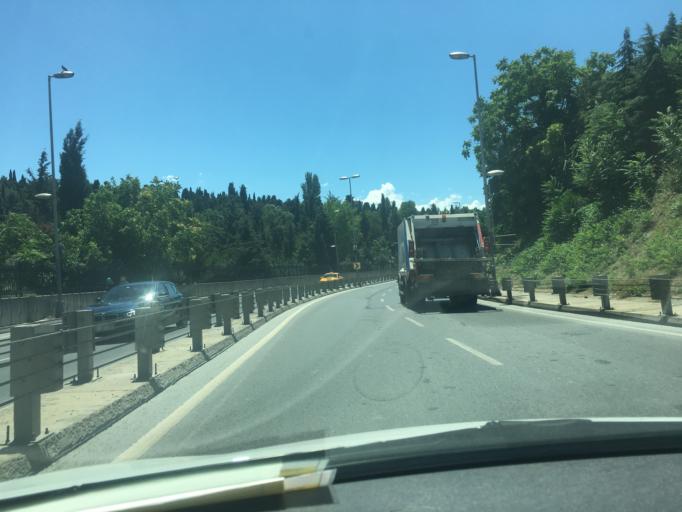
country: TR
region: Istanbul
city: Sisli
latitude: 41.0509
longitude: 28.9698
